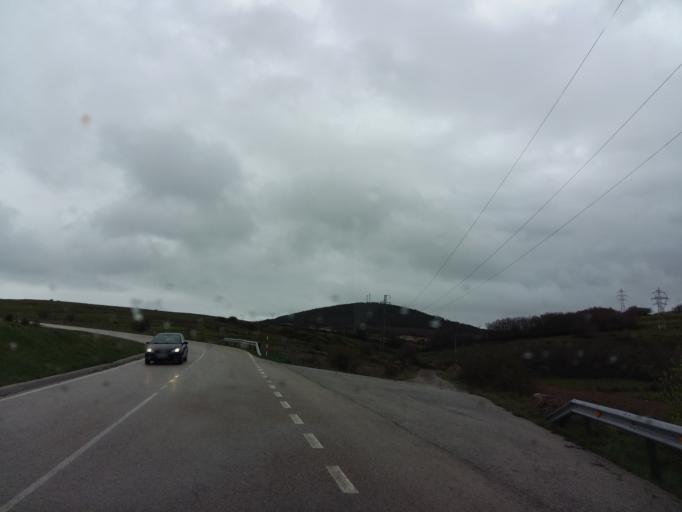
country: ES
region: Cantabria
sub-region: Provincia de Cantabria
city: Mataporquera
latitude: 42.8874
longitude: -4.1579
